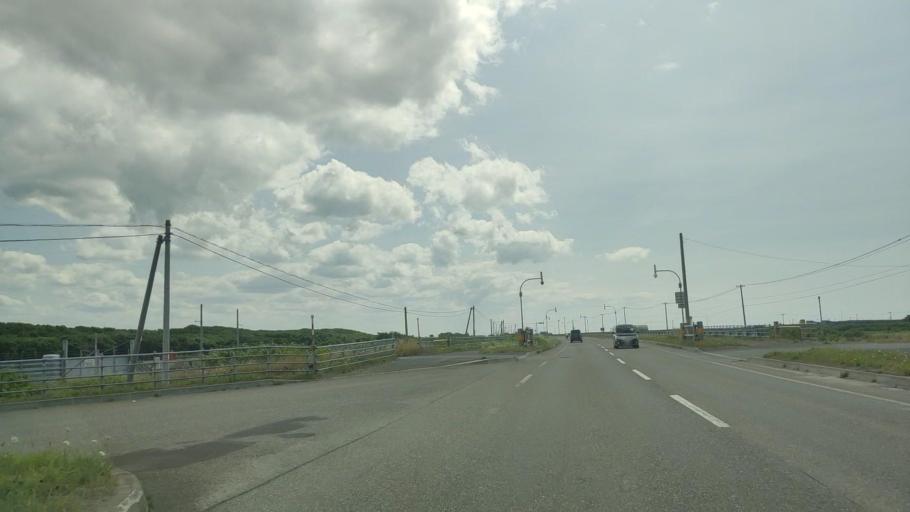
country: JP
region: Hokkaido
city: Makubetsu
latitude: 44.8711
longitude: 141.7520
